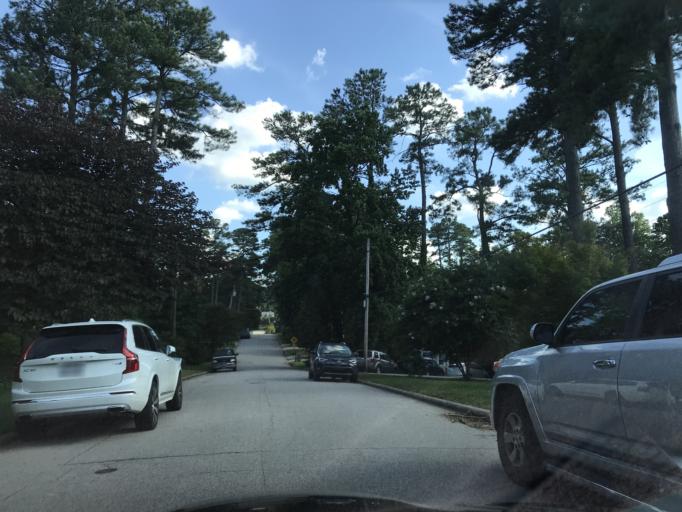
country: US
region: North Carolina
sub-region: Wake County
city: West Raleigh
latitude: 35.8043
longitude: -78.6723
